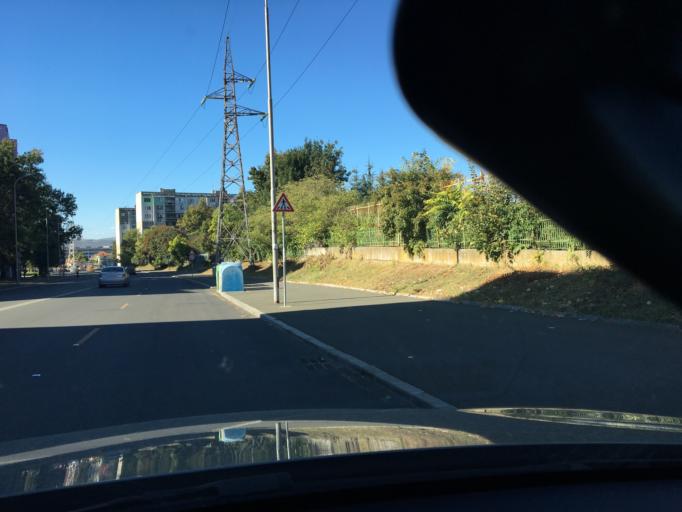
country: BG
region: Burgas
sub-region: Obshtina Burgas
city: Burgas
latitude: 42.5192
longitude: 27.4504
